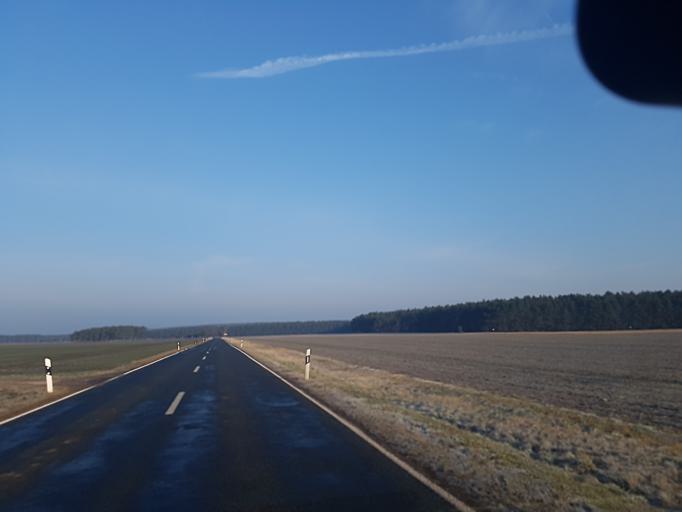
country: DE
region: Brandenburg
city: Golzow
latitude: 52.2490
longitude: 12.6925
